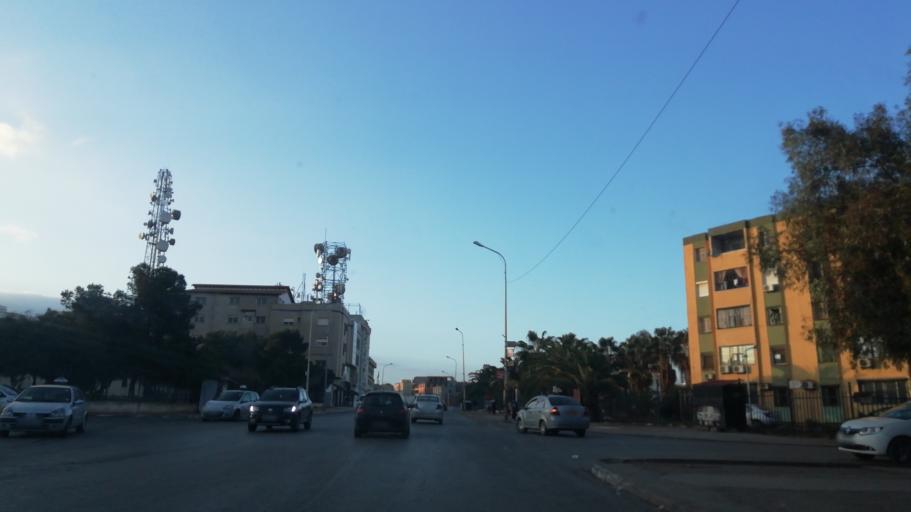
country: DZ
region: Oran
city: Oran
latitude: 35.6702
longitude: -0.6587
